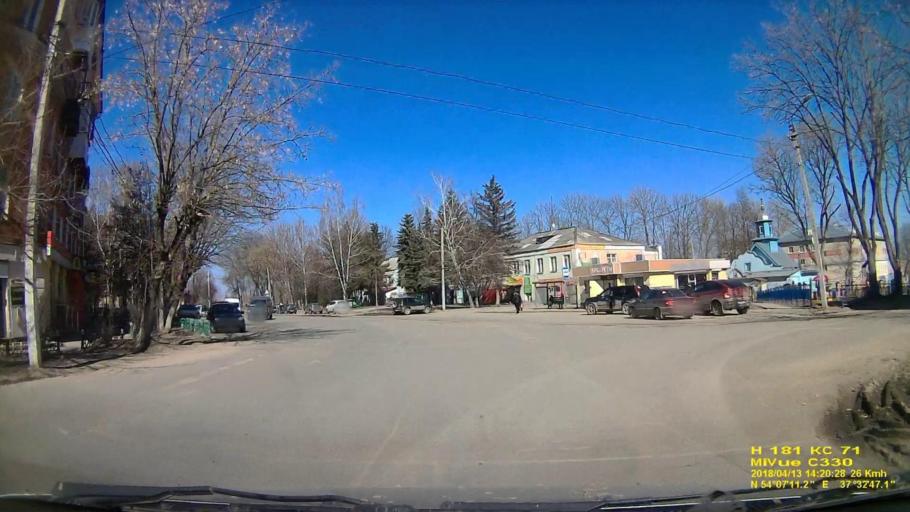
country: RU
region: Tula
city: Kosaya Gora
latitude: 54.1198
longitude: 37.5465
